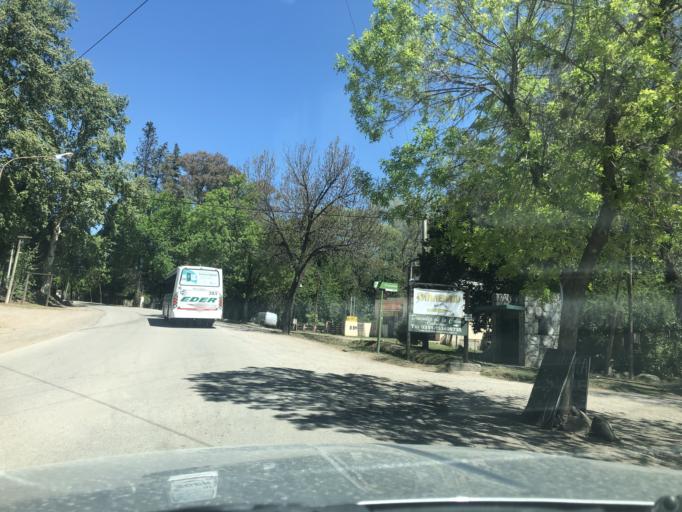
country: AR
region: Cordoba
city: La Granja
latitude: -31.0114
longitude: -64.2704
